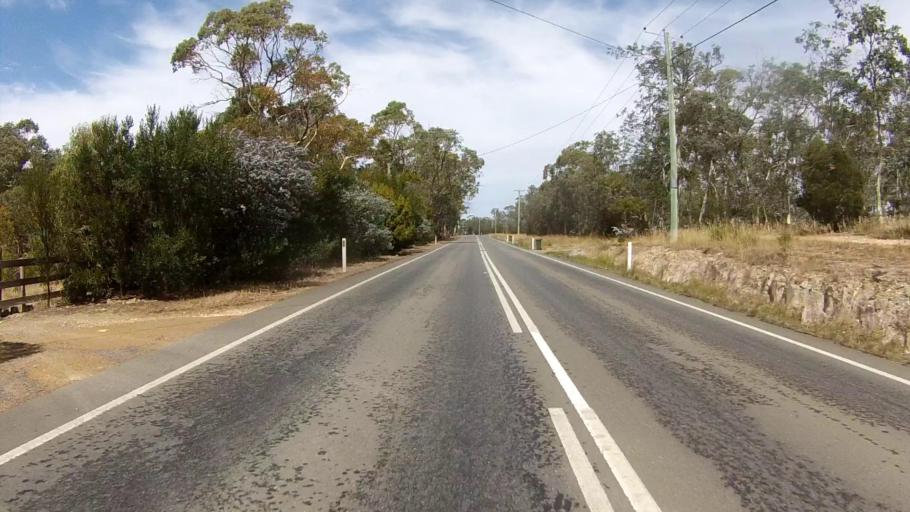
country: AU
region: Tasmania
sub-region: Clarence
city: Sandford
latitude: -42.9694
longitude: 147.5033
